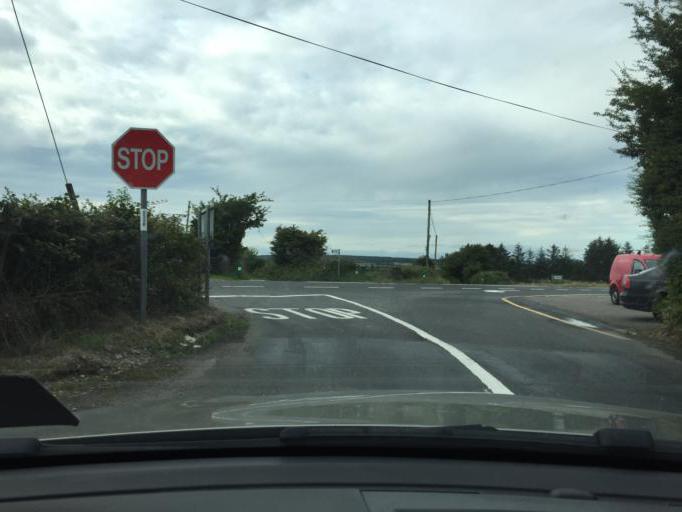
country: IE
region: Munster
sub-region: Waterford
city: Dungarvan
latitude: 52.0112
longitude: -7.7027
